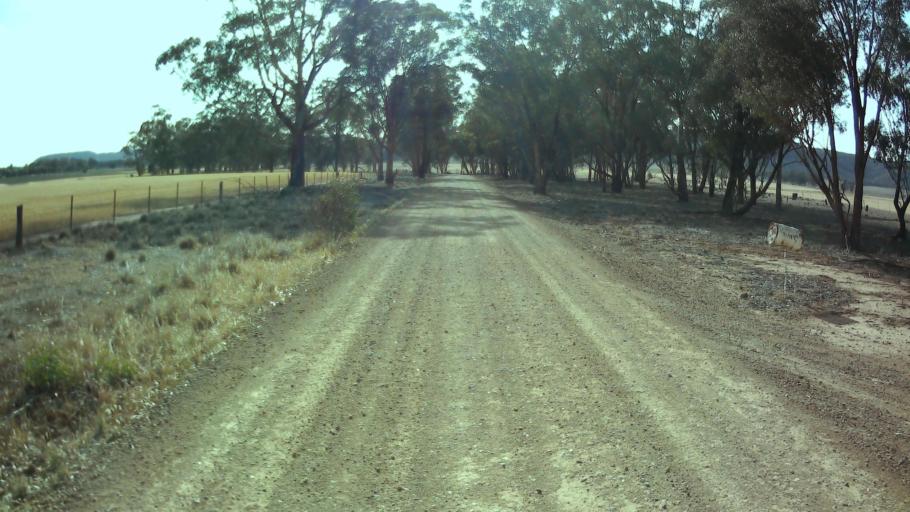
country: AU
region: New South Wales
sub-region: Weddin
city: Grenfell
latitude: -33.7975
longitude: 148.0913
